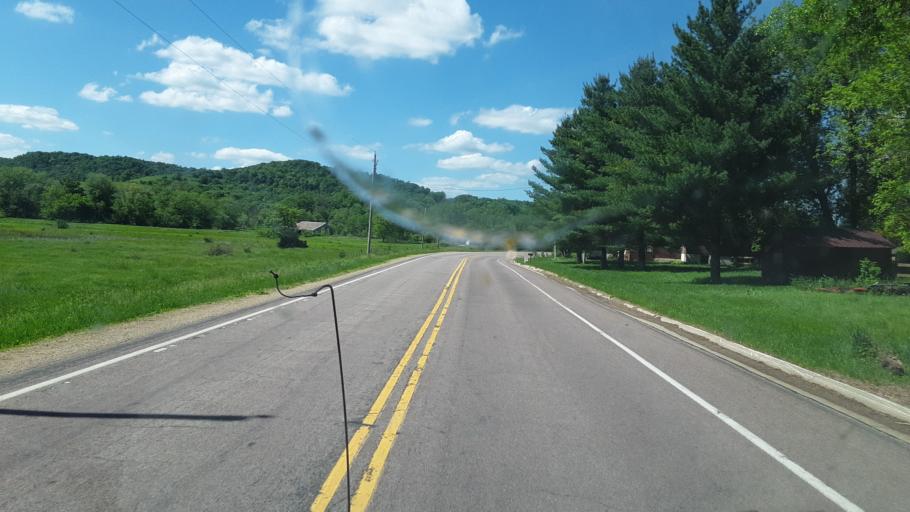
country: US
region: Wisconsin
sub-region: Richland County
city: Richland Center
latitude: 43.3695
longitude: -90.2663
